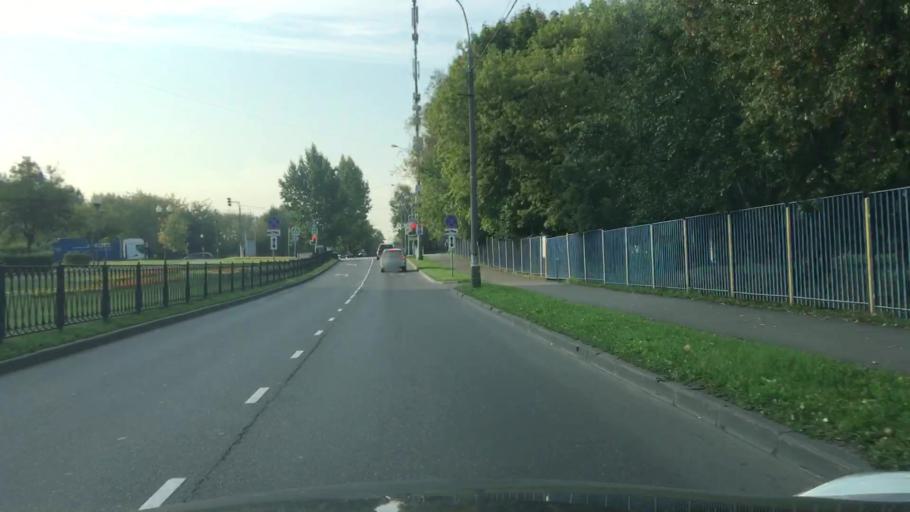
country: RU
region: Moscow
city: Davydkovo
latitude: 55.7207
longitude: 37.4612
